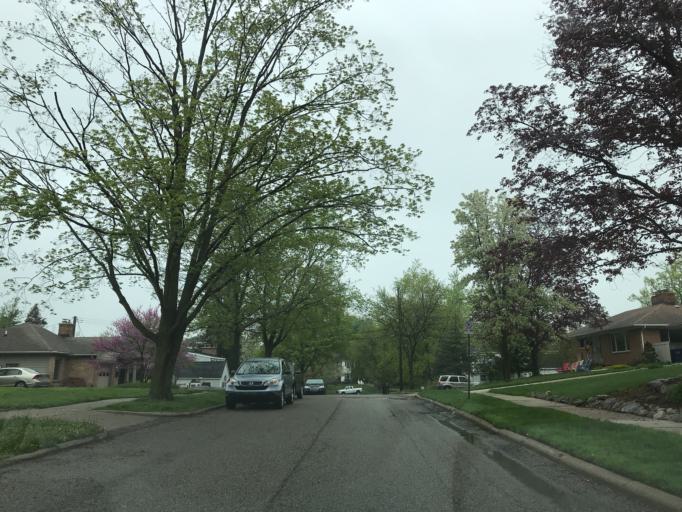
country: US
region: Michigan
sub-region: Washtenaw County
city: Ann Arbor
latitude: 42.2580
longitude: -83.7205
